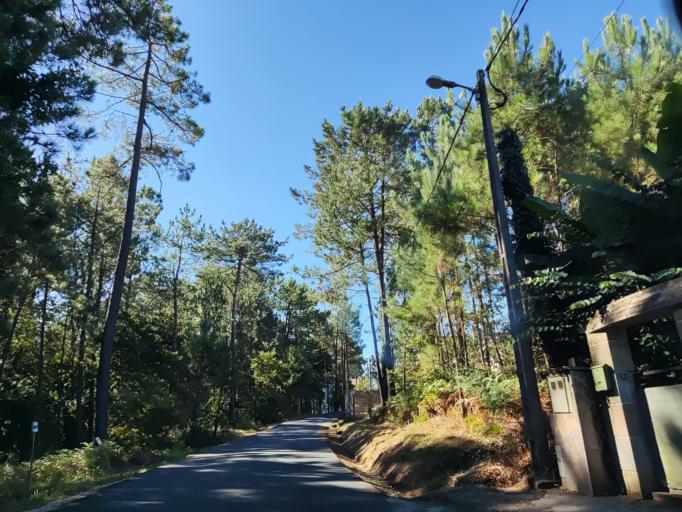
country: ES
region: Galicia
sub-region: Provincia da Coruna
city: Rianxo
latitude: 42.6880
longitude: -8.8475
